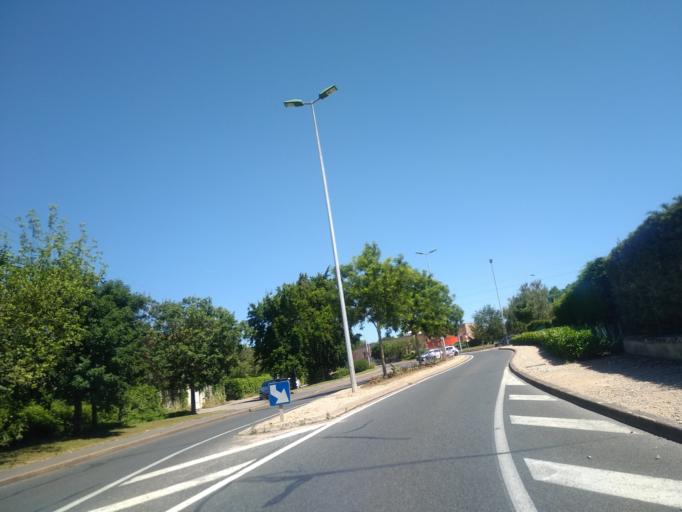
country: FR
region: Rhone-Alpes
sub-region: Departement du Rhone
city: Sathonay-Camp
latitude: 45.8145
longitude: 4.8634
